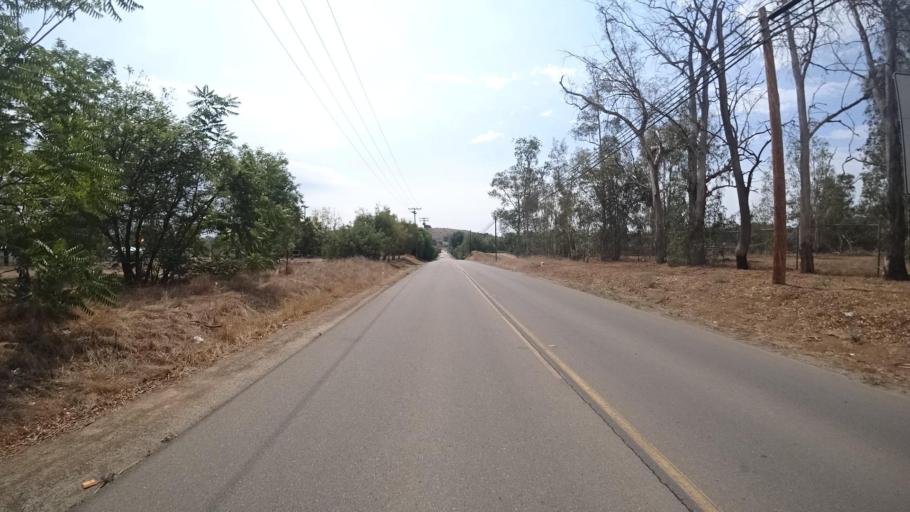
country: US
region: California
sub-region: San Diego County
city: Ramona
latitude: 33.0568
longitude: -116.8449
